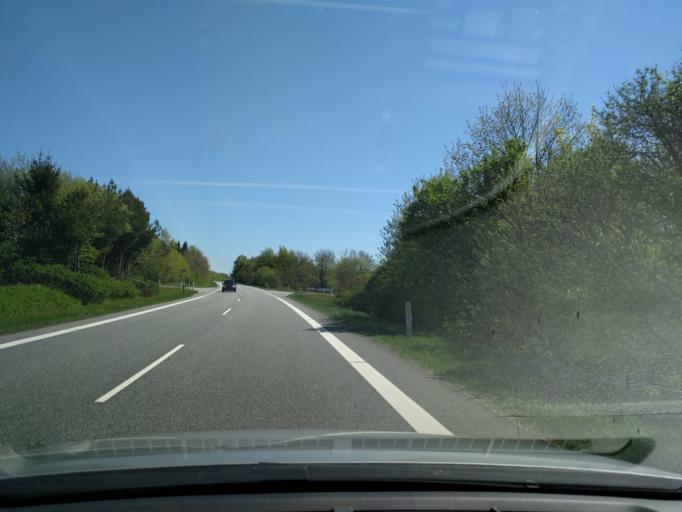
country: DK
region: South Denmark
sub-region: Vejen Kommune
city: Vejen
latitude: 55.5804
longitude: 9.1685
